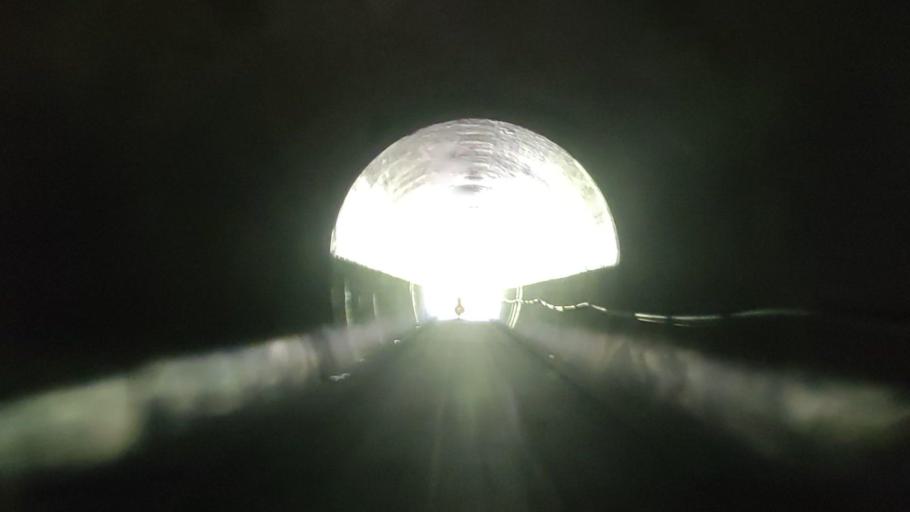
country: JP
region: Wakayama
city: Shingu
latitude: 33.9370
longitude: 135.9268
